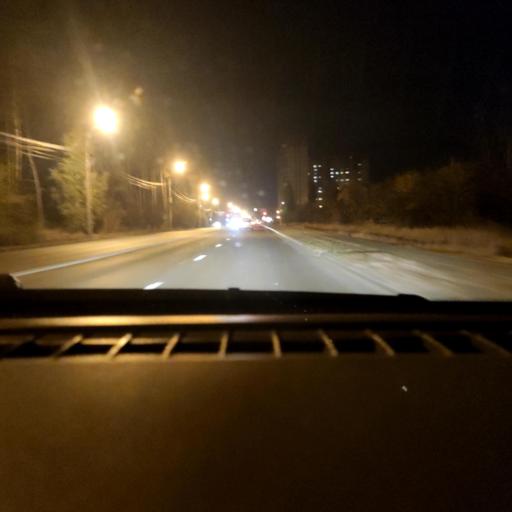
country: RU
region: Voronezj
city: Podgornoye
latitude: 51.7266
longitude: 39.1841
